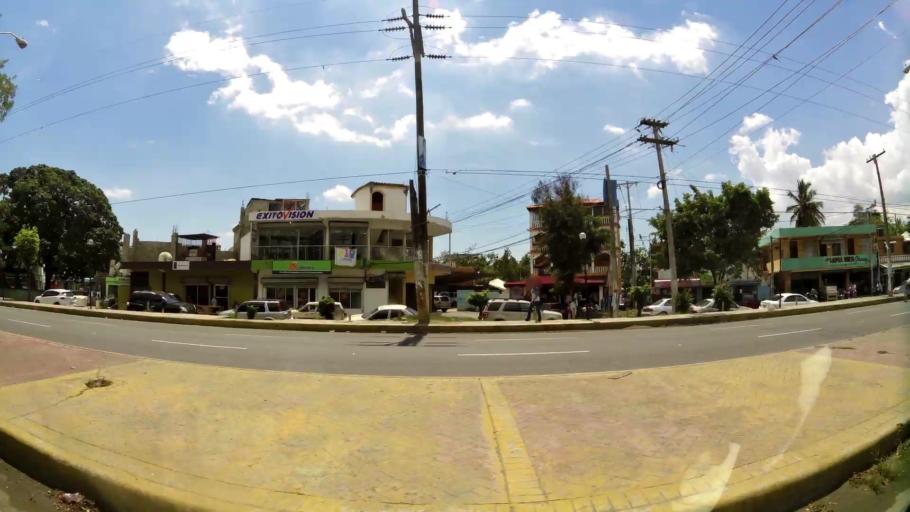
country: DO
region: Santo Domingo
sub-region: Santo Domingo
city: Santo Domingo Este
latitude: 18.5432
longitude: -69.8631
